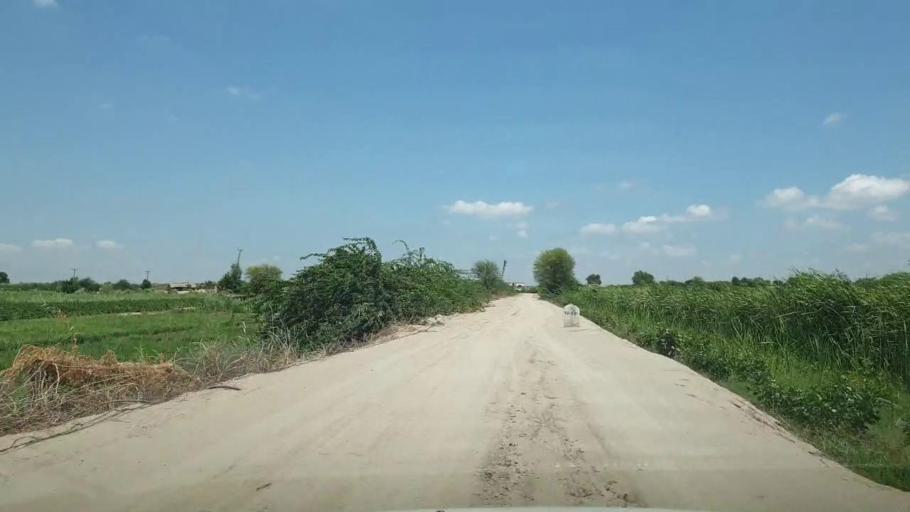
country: PK
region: Sindh
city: Sanghar
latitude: 26.1080
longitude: 69.0120
